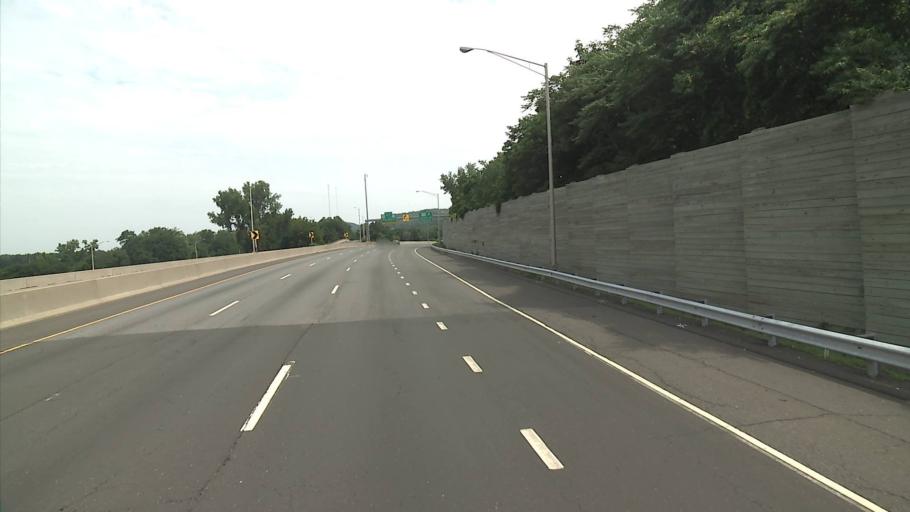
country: US
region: Connecticut
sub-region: Hartford County
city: Plainville
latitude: 41.6671
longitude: -72.8453
